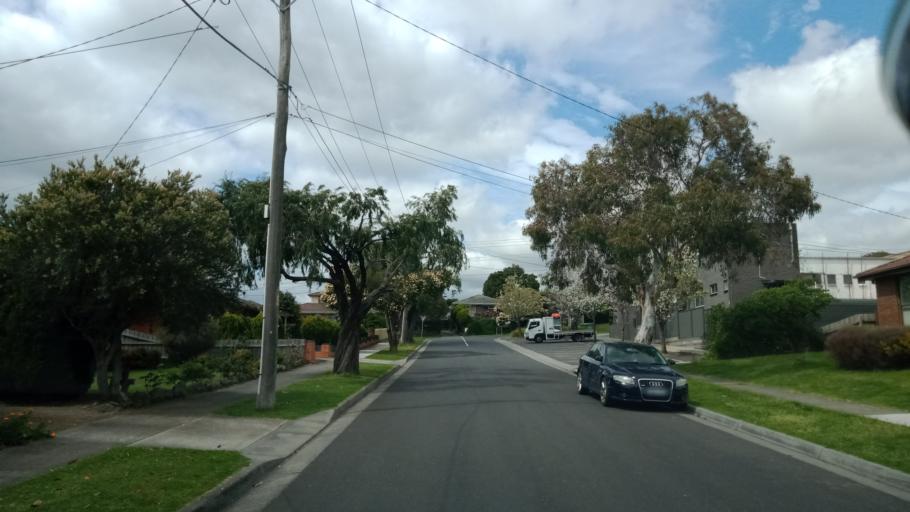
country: AU
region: Victoria
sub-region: Casey
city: Eumemmerring
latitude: -37.9950
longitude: 145.2498
